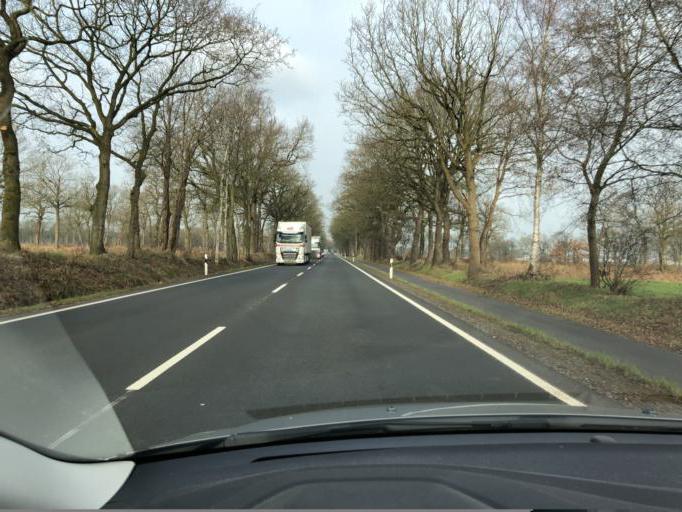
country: DE
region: Lower Saxony
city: Mittegrossefehn
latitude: 53.3643
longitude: 7.5923
